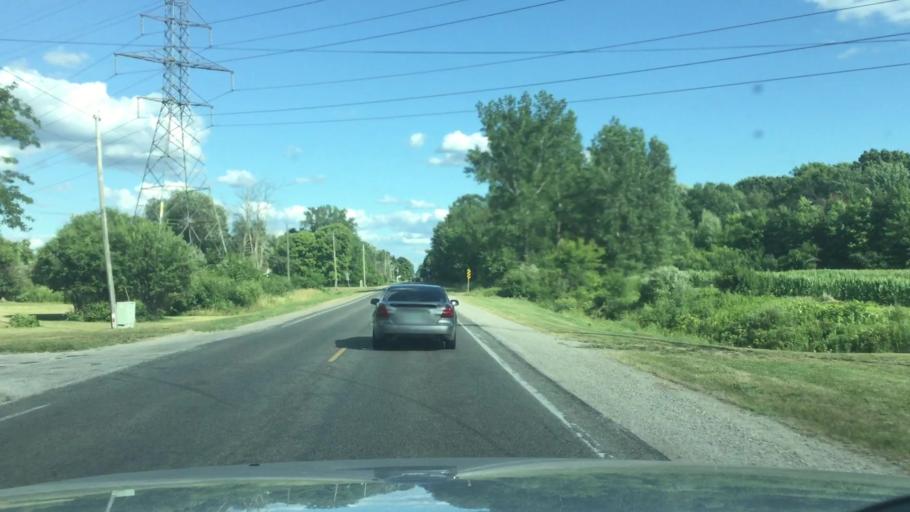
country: US
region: Michigan
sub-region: Saginaw County
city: Saginaw
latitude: 43.3869
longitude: -83.9290
